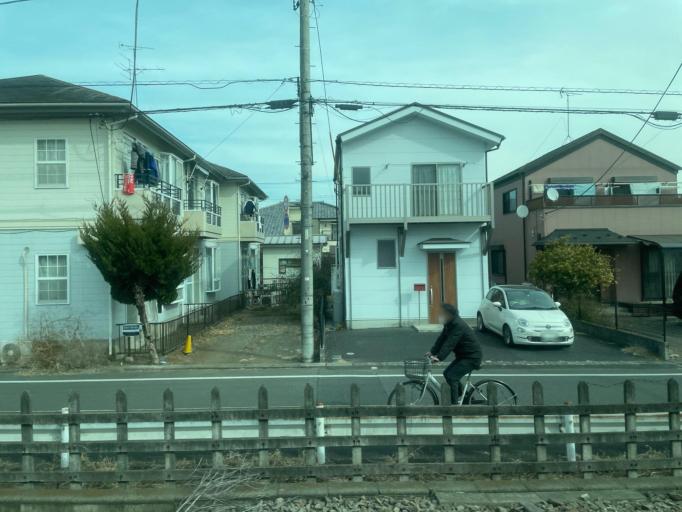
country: JP
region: Tokyo
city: Ome
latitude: 35.7816
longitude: 139.2912
